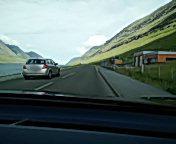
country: FO
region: Nordoyar
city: Klaksvik
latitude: 62.3022
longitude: -6.5231
